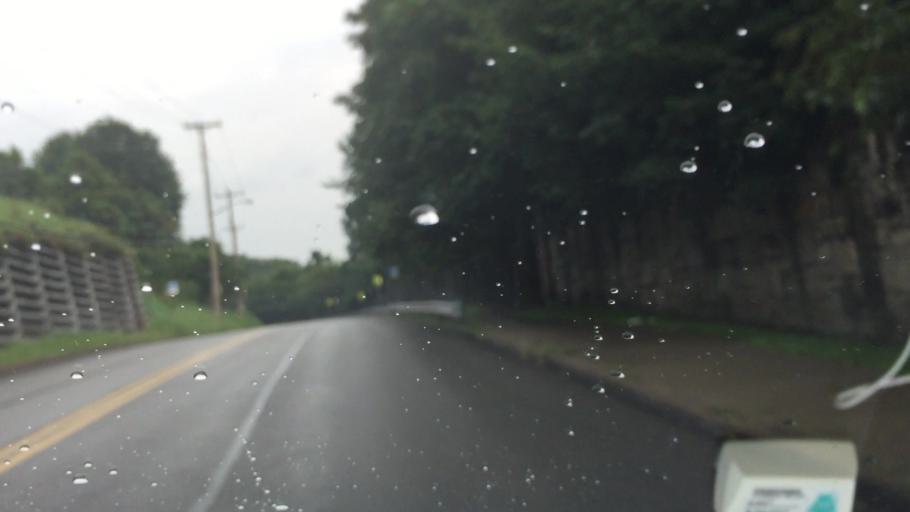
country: US
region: Pennsylvania
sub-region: Allegheny County
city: Bloomfield
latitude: 40.4779
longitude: -79.9482
